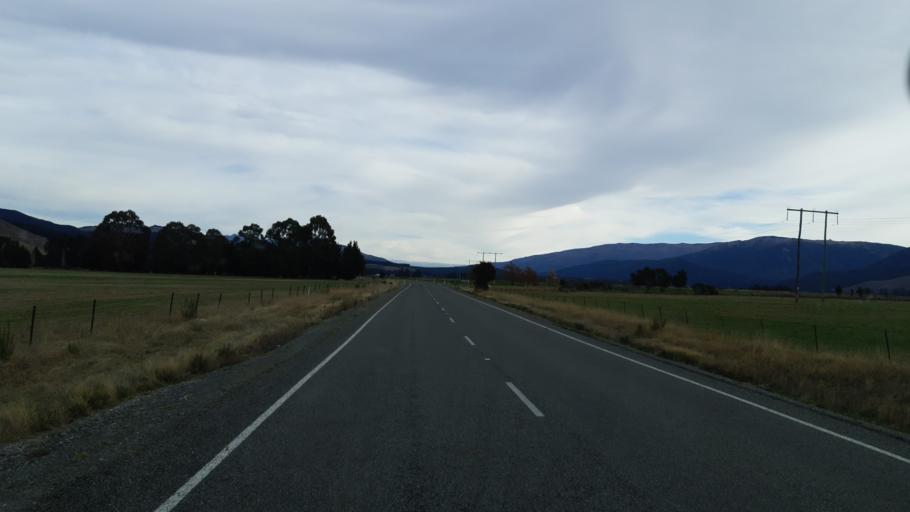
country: NZ
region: Tasman
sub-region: Tasman District
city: Brightwater
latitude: -41.6428
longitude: 173.3029
